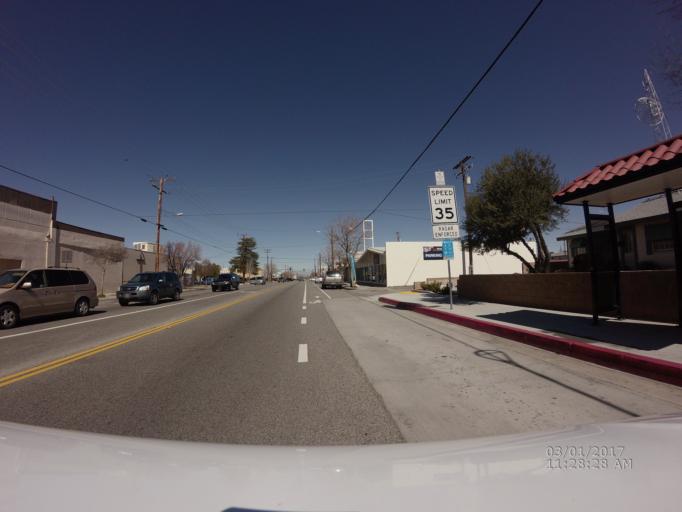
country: US
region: California
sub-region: Los Angeles County
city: Quartz Hill
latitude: 34.6459
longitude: -118.2184
